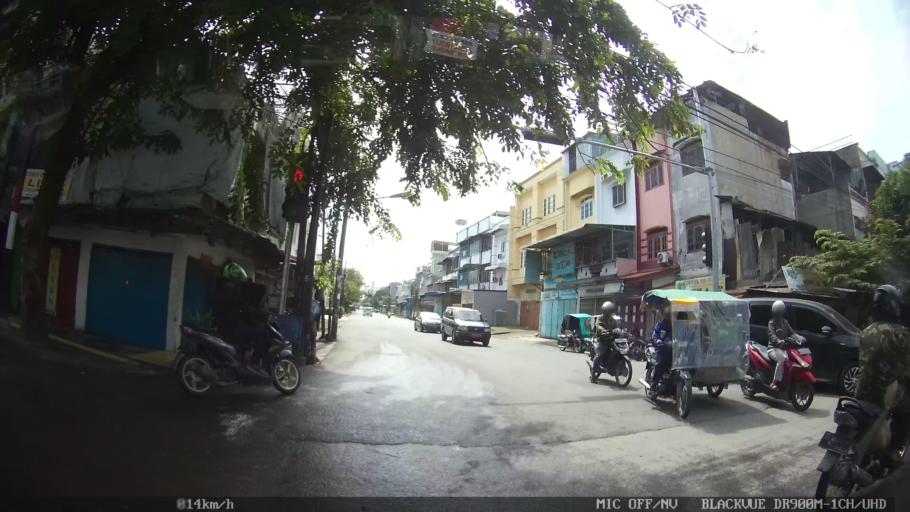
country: ID
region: North Sumatra
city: Medan
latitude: 3.5950
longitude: 98.7065
